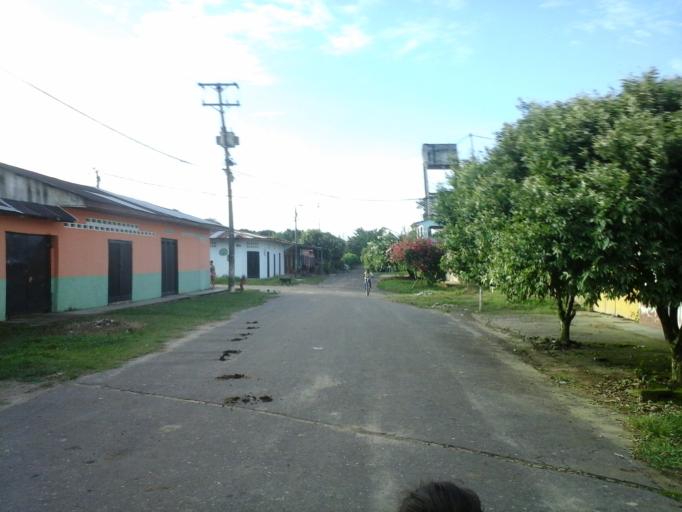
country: CO
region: Caqueta
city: El Doncello
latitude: 1.6117
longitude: -74.9945
